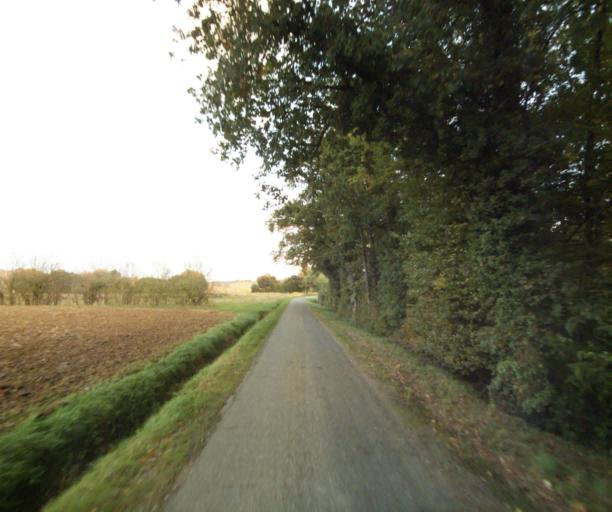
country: FR
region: Midi-Pyrenees
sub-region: Departement du Gers
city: Vic-Fezensac
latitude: 43.7839
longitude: 0.2506
